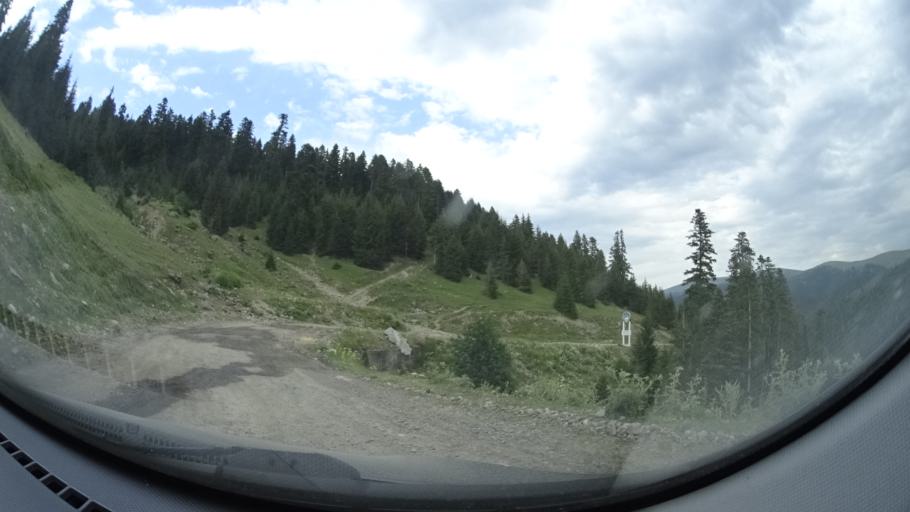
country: GE
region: Samtskhe-Javakheti
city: Adigeni
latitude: 41.6309
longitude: 42.5676
